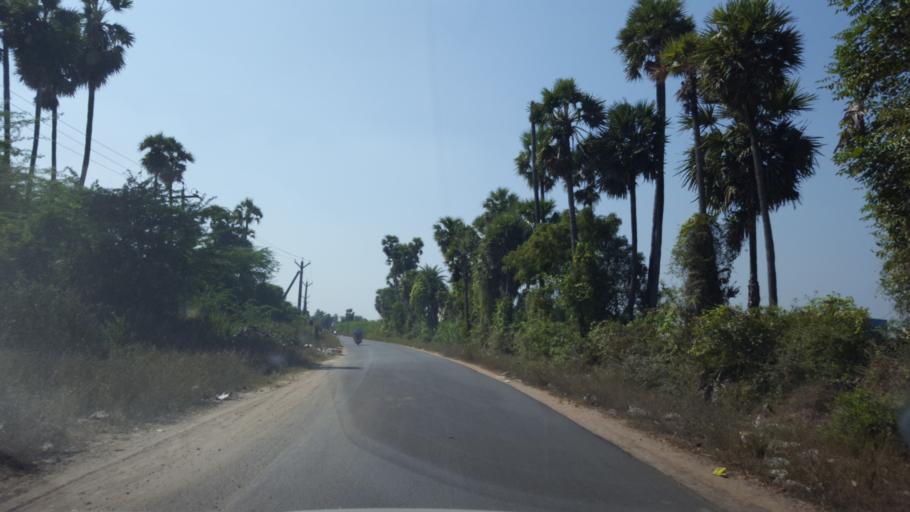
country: IN
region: Tamil Nadu
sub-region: Kancheepuram
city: Kanchipuram
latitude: 12.8383
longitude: 79.7274
